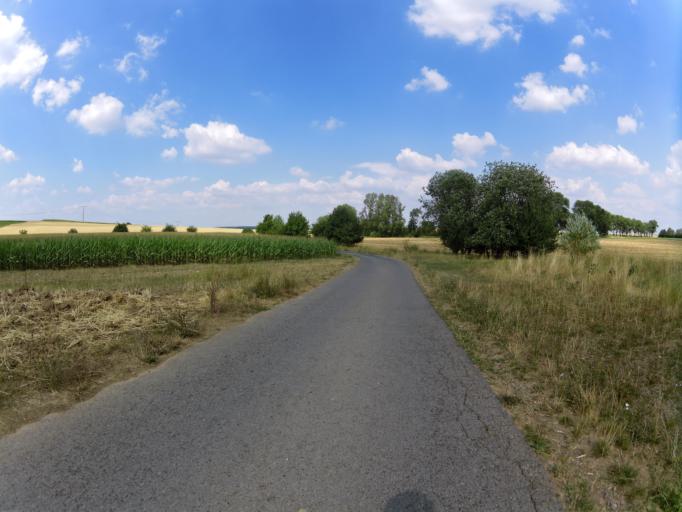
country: DE
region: Bavaria
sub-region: Regierungsbezirk Unterfranken
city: Ochsenfurt
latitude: 49.6423
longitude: 10.0572
